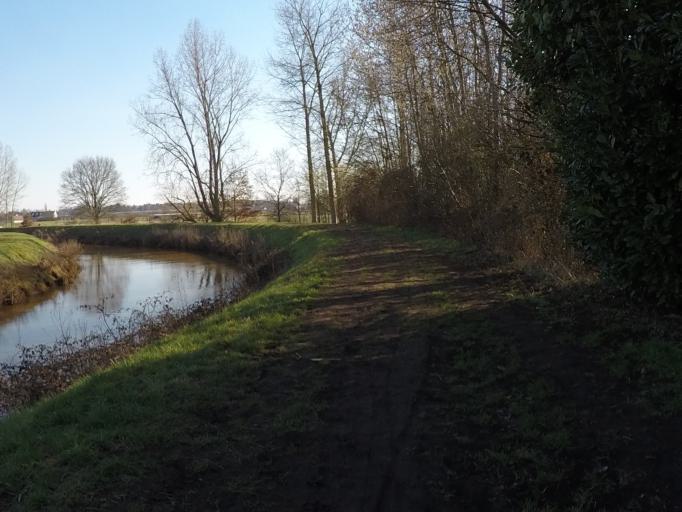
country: BE
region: Flanders
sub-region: Provincie Antwerpen
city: Heist-op-den-Berg
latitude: 51.1083
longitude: 4.7369
